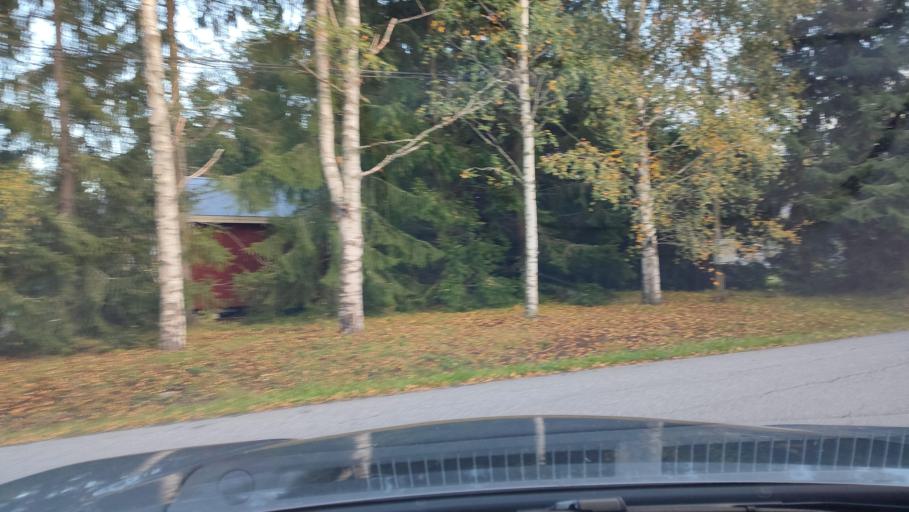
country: FI
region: Ostrobothnia
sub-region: Sydosterbotten
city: Kristinestad
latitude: 62.2461
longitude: 21.5166
